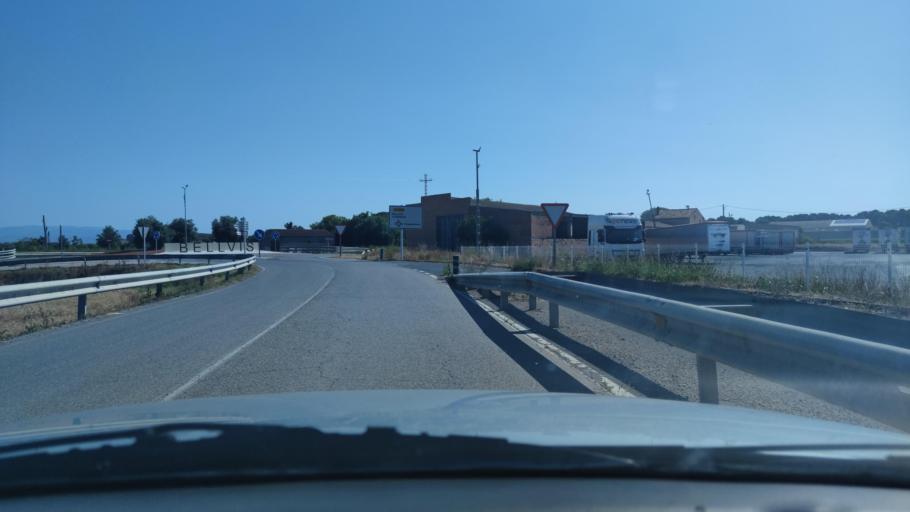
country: ES
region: Catalonia
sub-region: Provincia de Lleida
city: Bellvis
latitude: 41.6655
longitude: 0.8118
